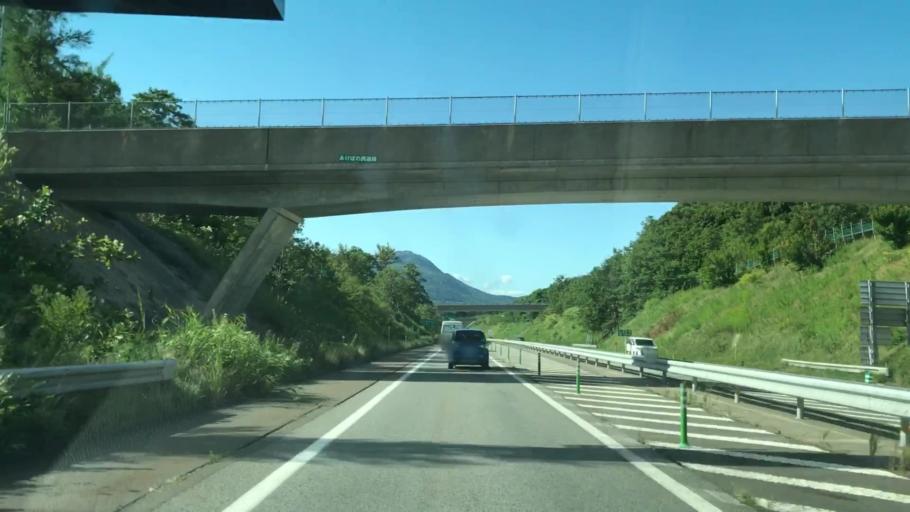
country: JP
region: Hokkaido
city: Date
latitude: 42.4764
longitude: 140.9019
